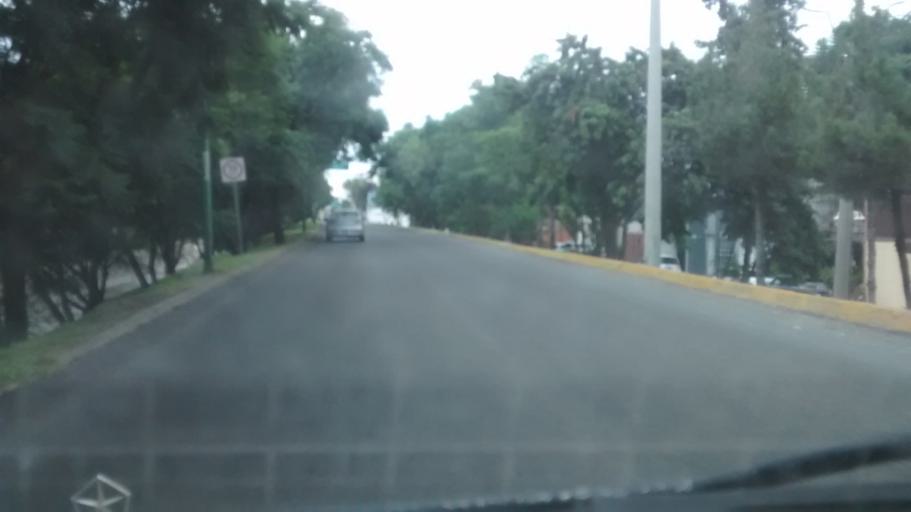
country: MX
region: Guanajuato
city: Leon
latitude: 21.1132
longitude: -101.6646
